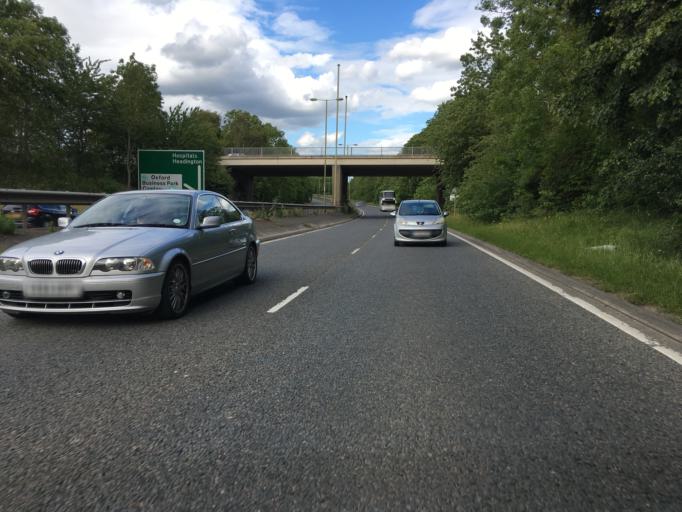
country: GB
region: England
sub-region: Oxfordshire
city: Cowley
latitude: 51.7247
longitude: -1.2104
